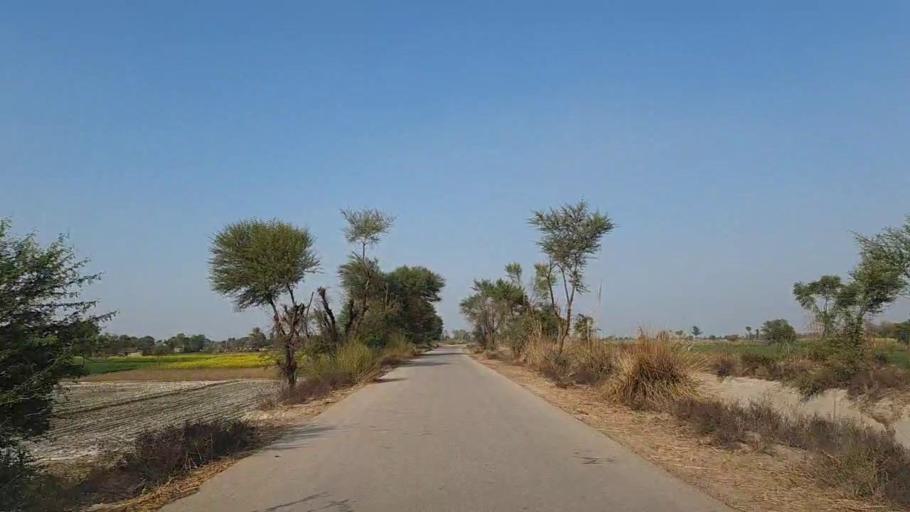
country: PK
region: Sindh
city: Daur
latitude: 26.4162
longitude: 68.2595
